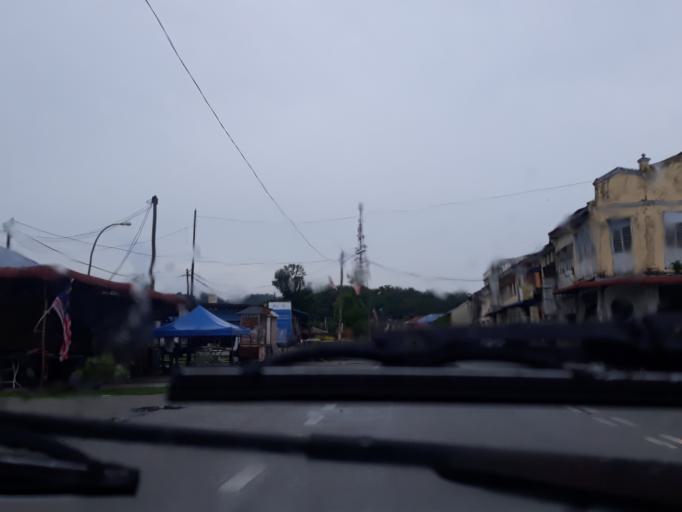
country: MY
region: Penang
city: Nibong Tebal
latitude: 5.2113
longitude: 100.6125
